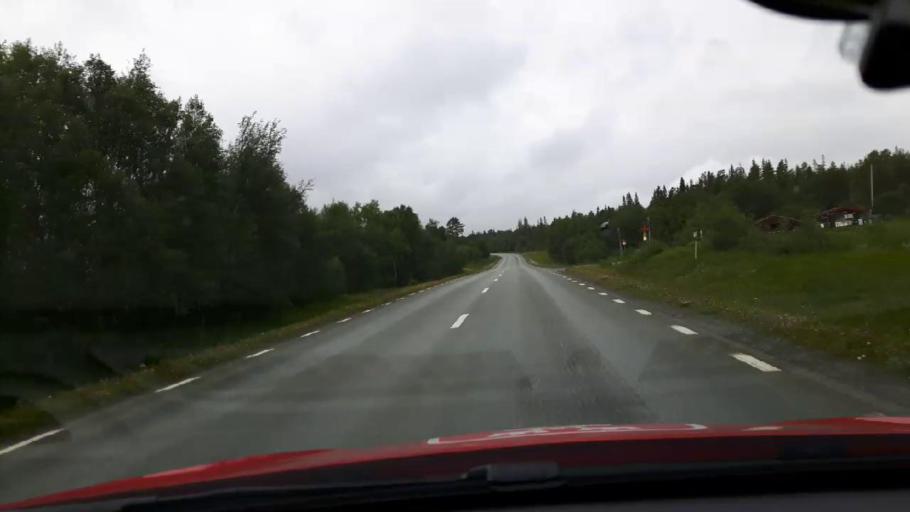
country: NO
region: Nord-Trondelag
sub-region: Meraker
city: Meraker
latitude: 63.2911
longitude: 12.1211
